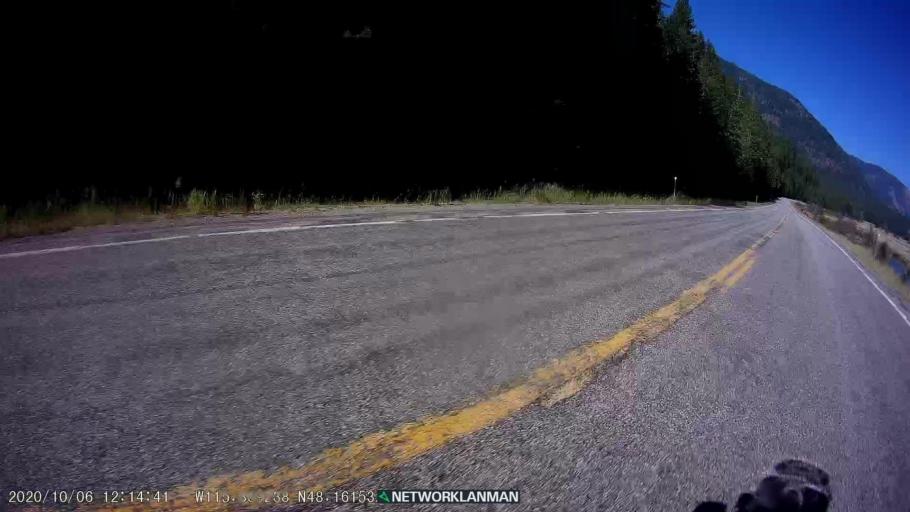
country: US
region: Montana
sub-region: Lincoln County
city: Libby
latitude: 48.1619
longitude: -115.8693
